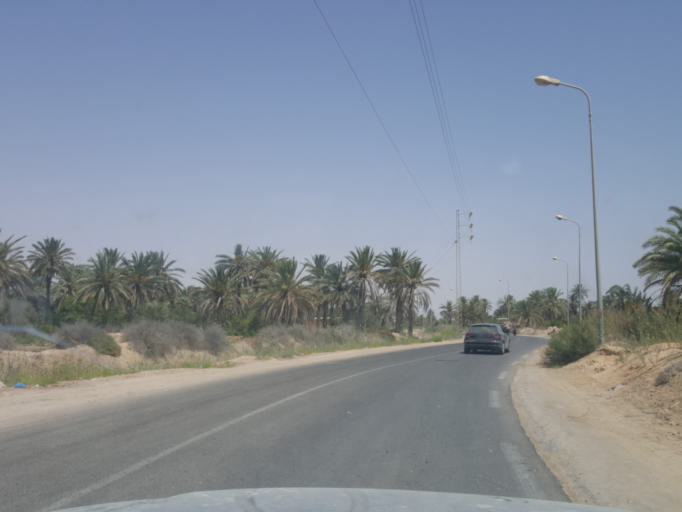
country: TN
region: Qabis
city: Gabes
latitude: 33.9646
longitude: 9.9994
